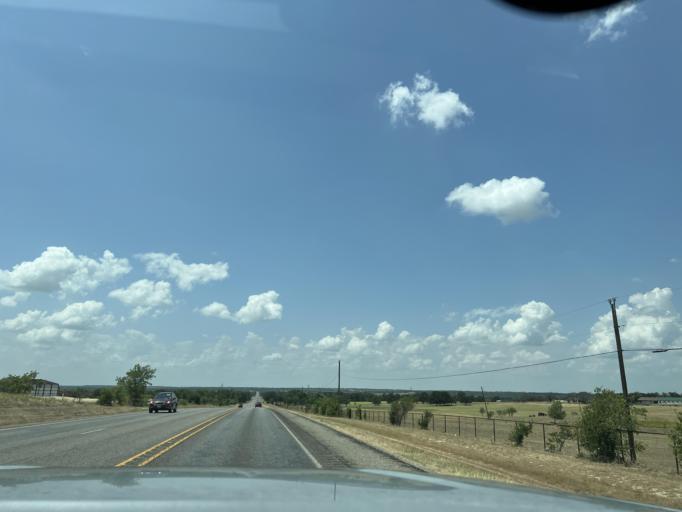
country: US
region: Texas
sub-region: Parker County
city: Springtown
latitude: 32.8922
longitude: -97.7324
